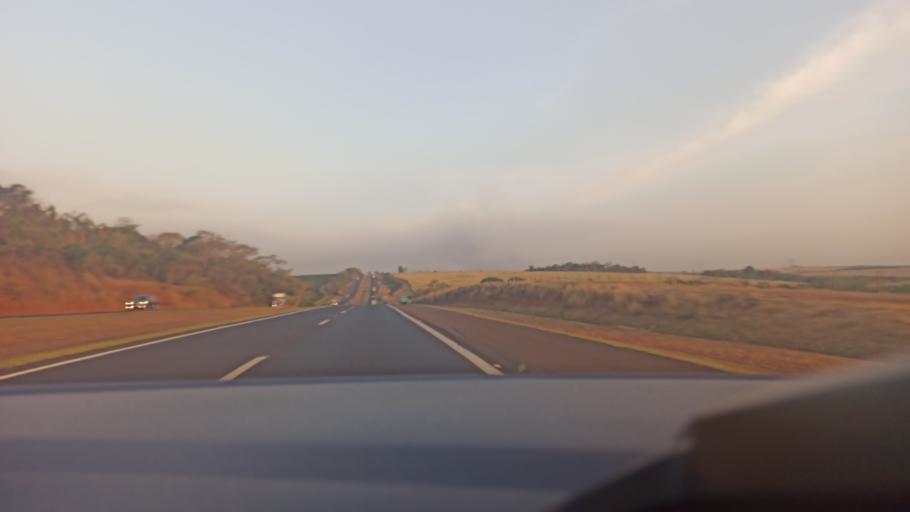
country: BR
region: Sao Paulo
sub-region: Taquaritinga
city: Taquaritinga
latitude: -21.4314
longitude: -48.6627
